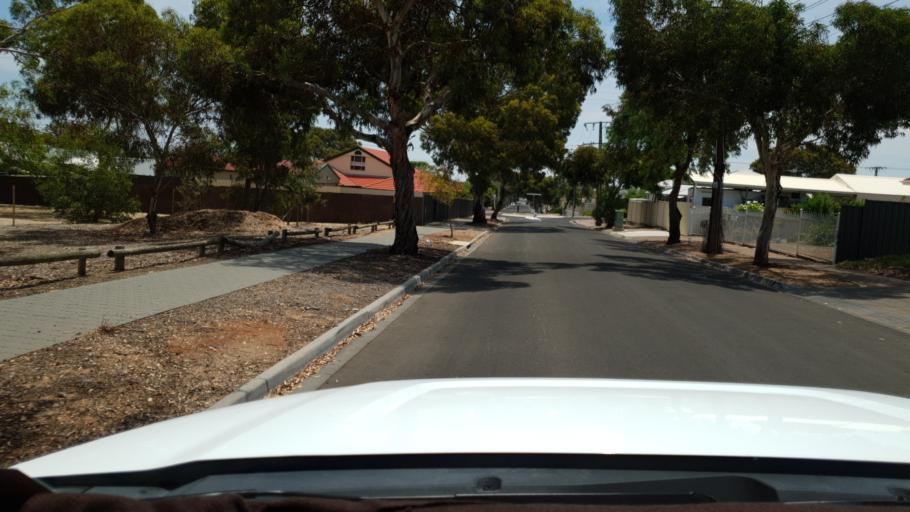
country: AU
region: South Australia
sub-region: Marion
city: Clovelly Park
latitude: -35.0069
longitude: 138.5813
